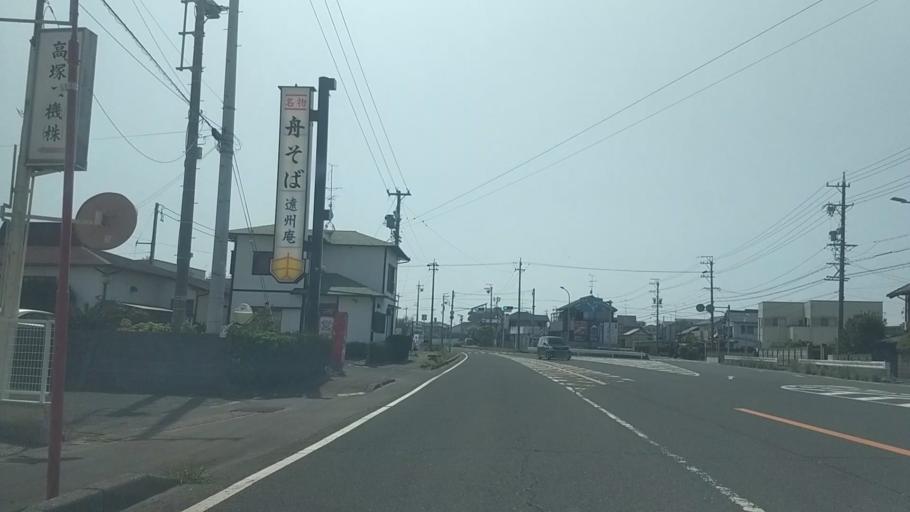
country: JP
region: Shizuoka
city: Hamamatsu
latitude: 34.6878
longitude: 137.6754
